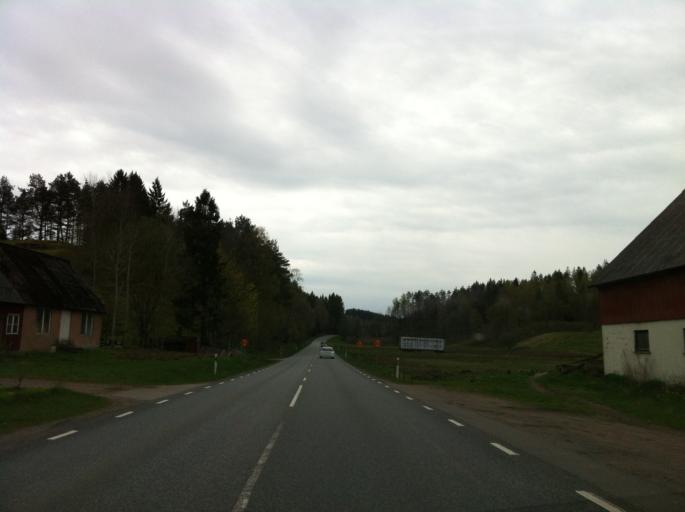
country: SE
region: Halland
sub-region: Halmstads Kommun
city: Getinge
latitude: 57.1241
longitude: 12.7102
